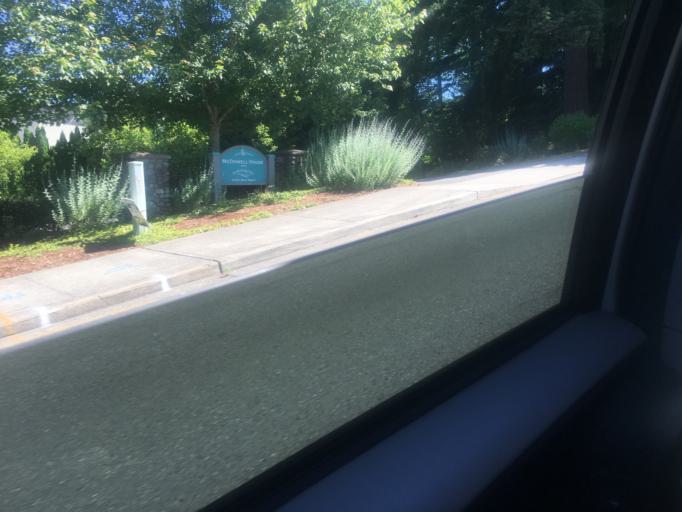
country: US
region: Washington
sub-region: King County
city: Bellevue
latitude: 47.6100
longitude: -122.1831
